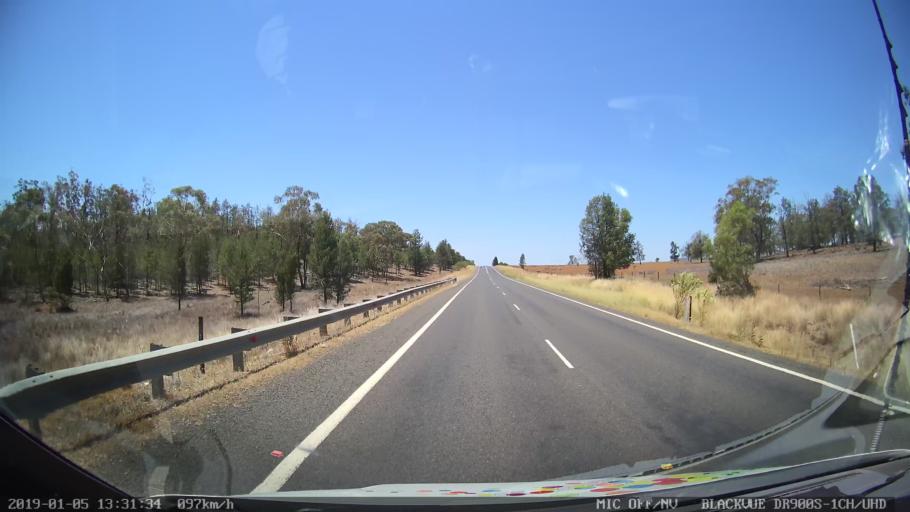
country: AU
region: New South Wales
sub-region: Gunnedah
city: Gunnedah
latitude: -31.0096
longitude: 150.0858
